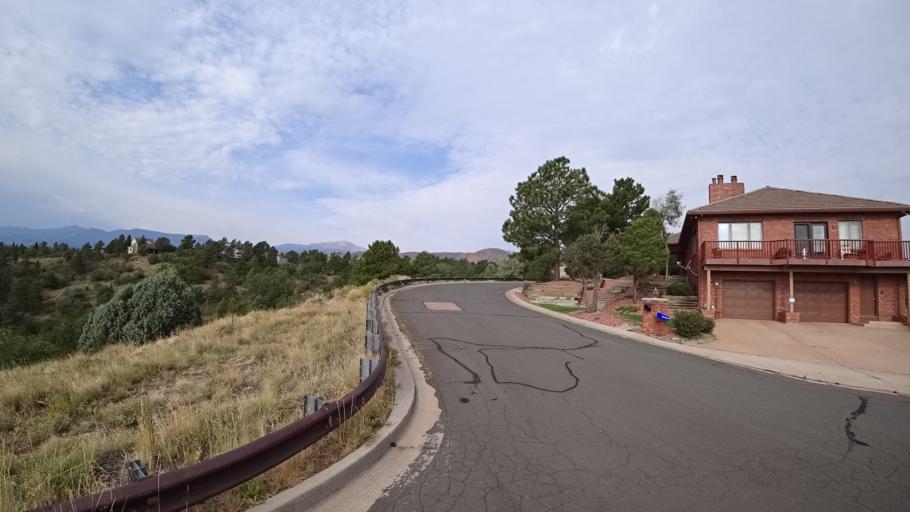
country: US
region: Colorado
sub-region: El Paso County
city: Air Force Academy
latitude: 38.9326
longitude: -104.8516
